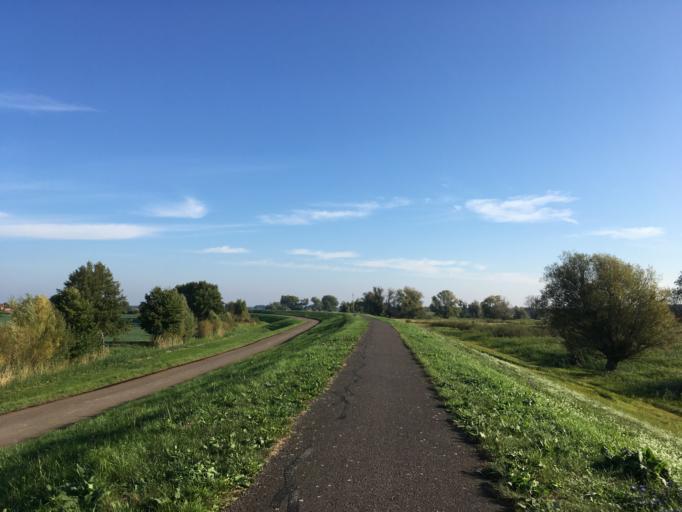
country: DE
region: Brandenburg
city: Reitwein
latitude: 52.4529
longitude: 14.5878
